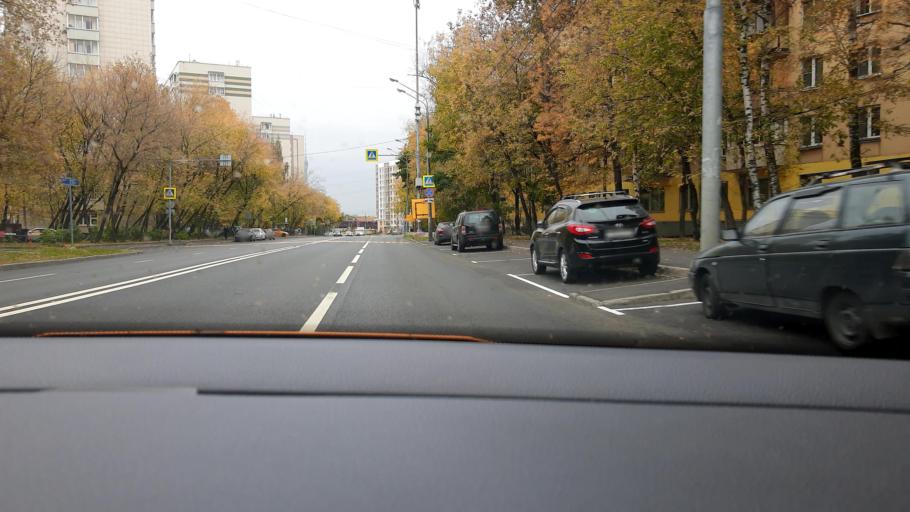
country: RU
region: Moscow
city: Leonovo
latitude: 55.8491
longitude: 37.6452
